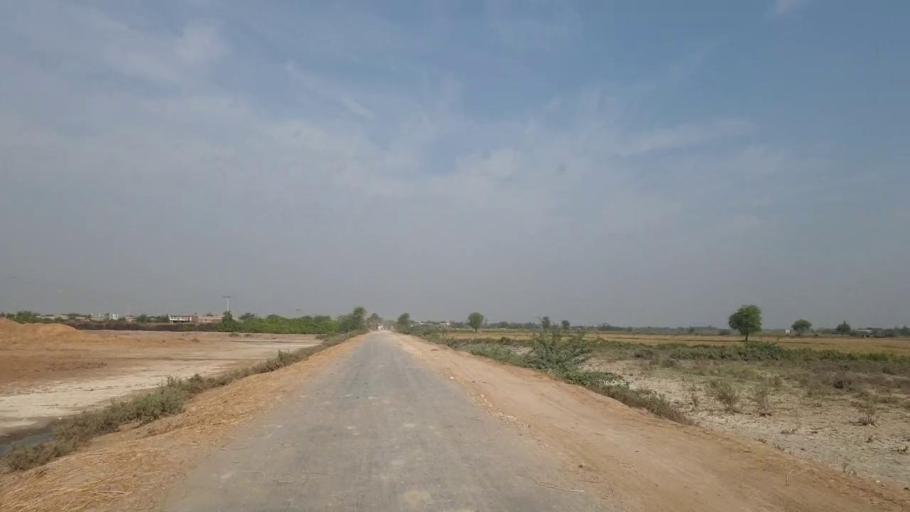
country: PK
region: Sindh
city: Tando Bago
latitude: 24.9074
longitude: 68.9966
